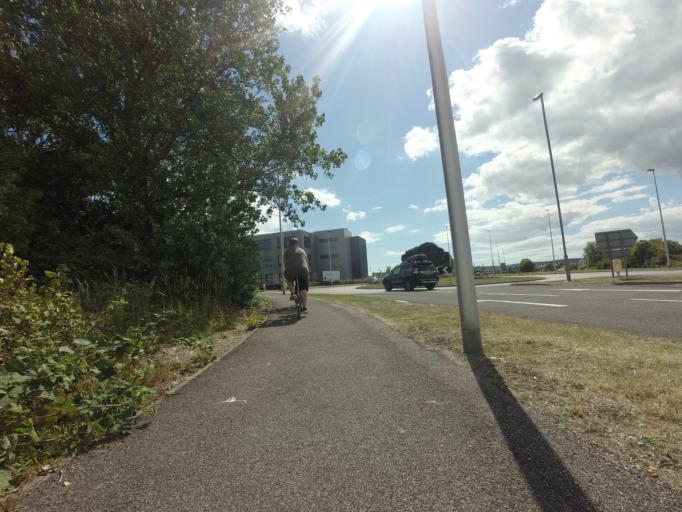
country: GB
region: England
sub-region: East Sussex
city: Pevensey
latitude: 50.7995
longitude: 0.3276
